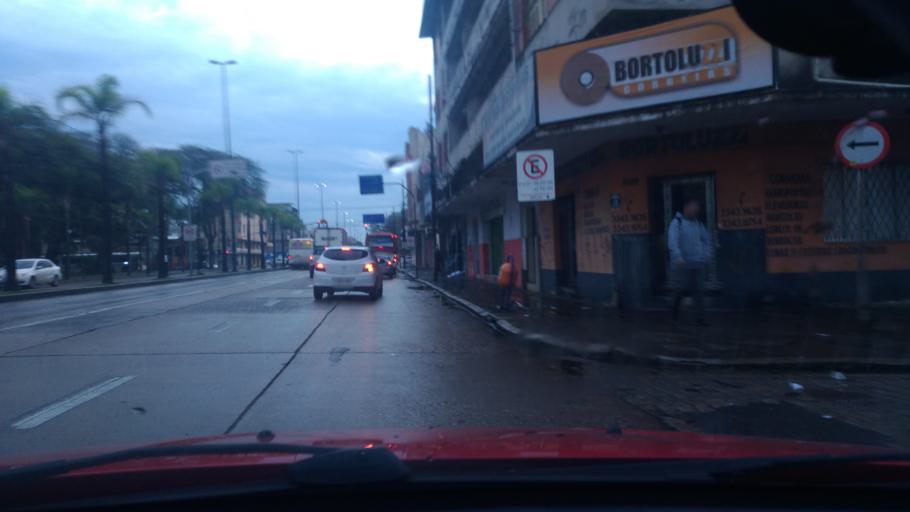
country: BR
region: Rio Grande do Sul
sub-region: Porto Alegre
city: Porto Alegre
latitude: -30.0064
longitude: -51.2010
